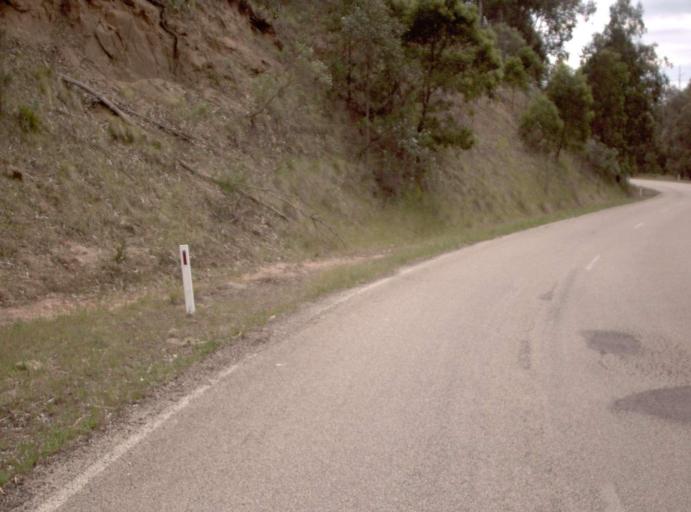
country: AU
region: Victoria
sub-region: East Gippsland
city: Bairnsdale
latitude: -37.5916
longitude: 147.1836
